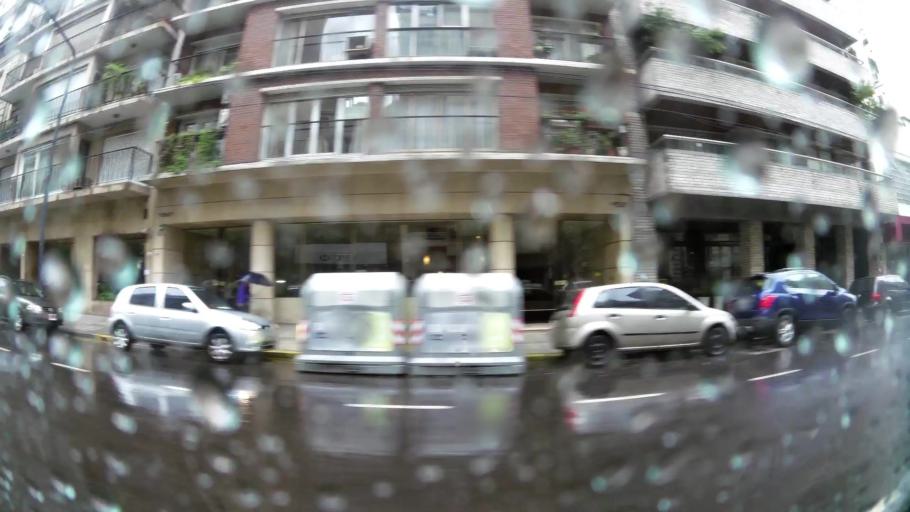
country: AR
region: Buenos Aires F.D.
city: Retiro
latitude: -34.5906
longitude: -58.3905
